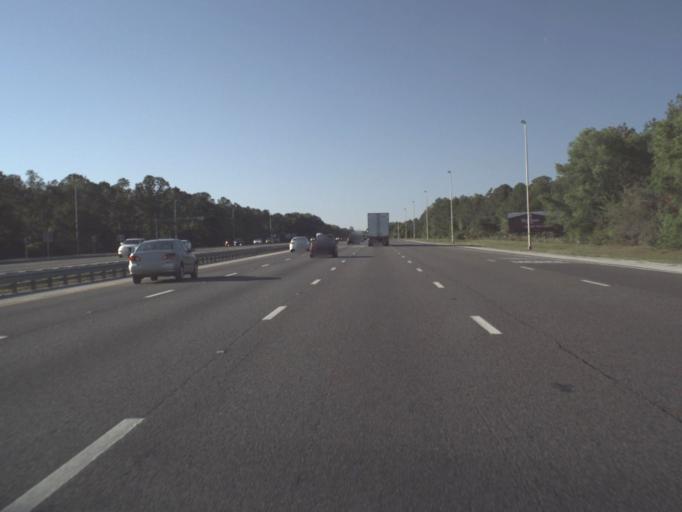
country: US
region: Florida
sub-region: Flagler County
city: Palm Coast
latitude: 29.5158
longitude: -81.1988
